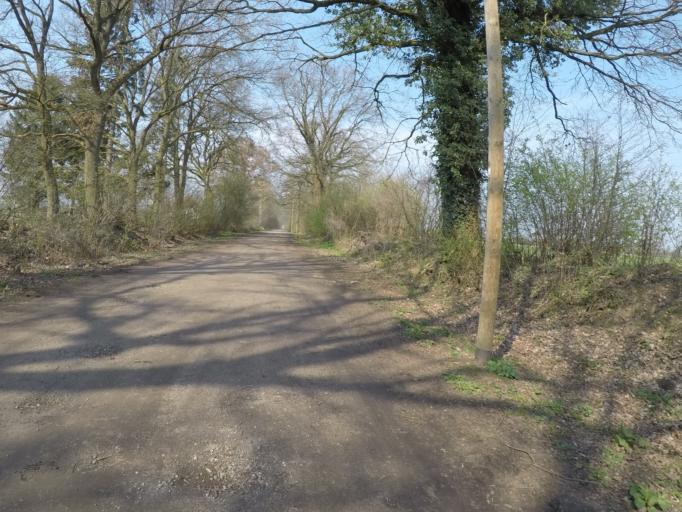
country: DE
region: Hamburg
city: Duvenstedt
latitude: 53.7180
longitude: 10.1003
